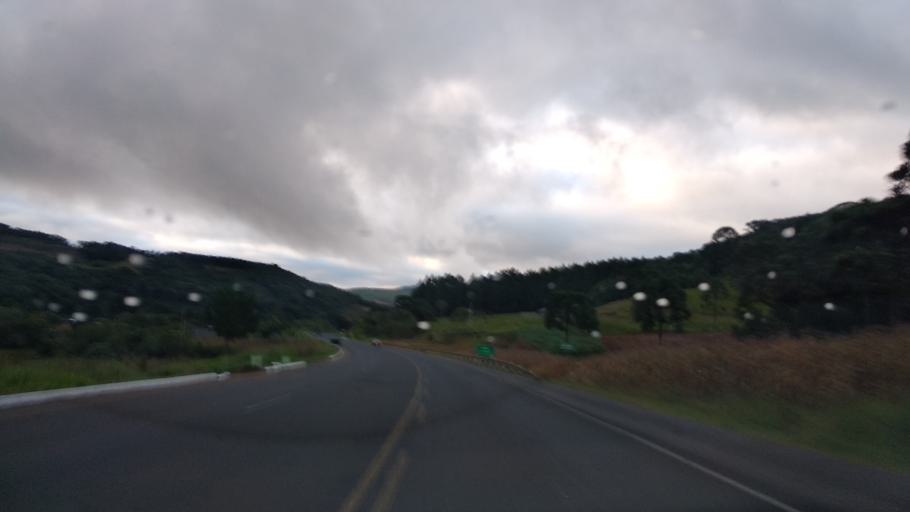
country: BR
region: Santa Catarina
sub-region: Campos Novos
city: Campos Novos
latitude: -27.4507
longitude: -50.9950
